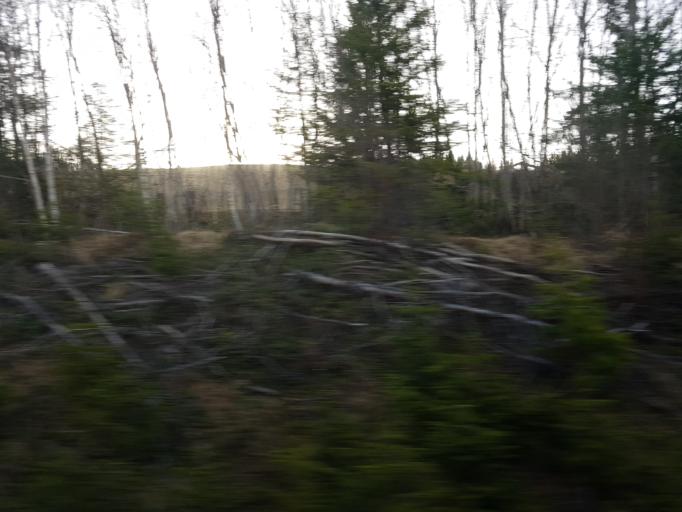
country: NO
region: Sor-Trondelag
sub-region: Rennebu
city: Berkak
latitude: 62.8531
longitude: 10.0240
